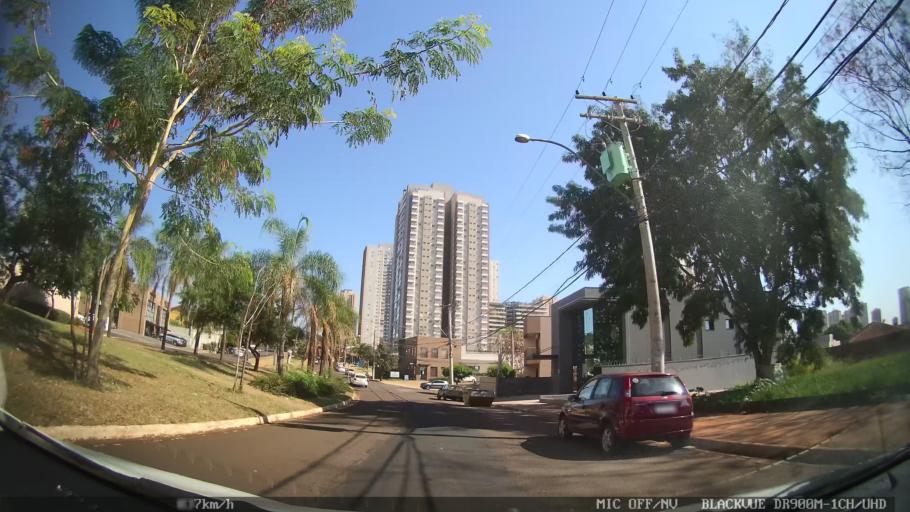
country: BR
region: Sao Paulo
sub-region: Ribeirao Preto
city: Ribeirao Preto
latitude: -21.2192
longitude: -47.7967
